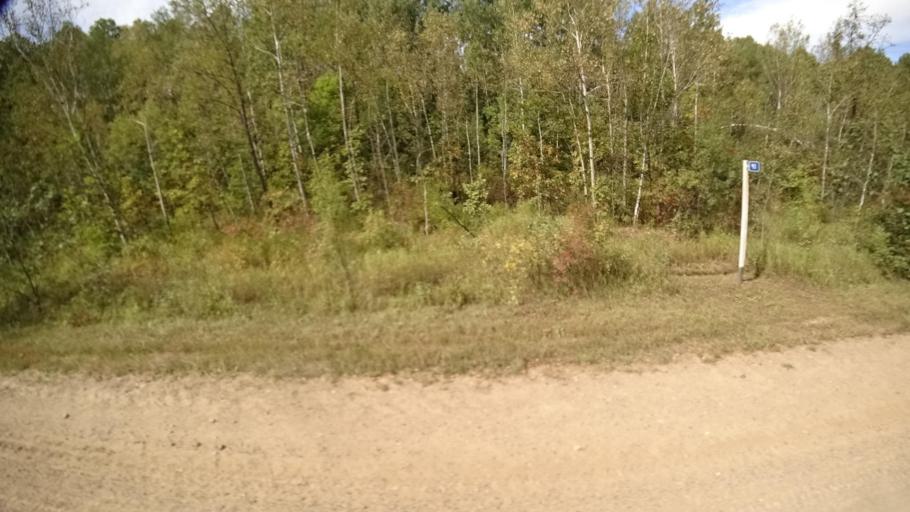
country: RU
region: Primorskiy
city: Yakovlevka
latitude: 44.6776
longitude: 133.6133
